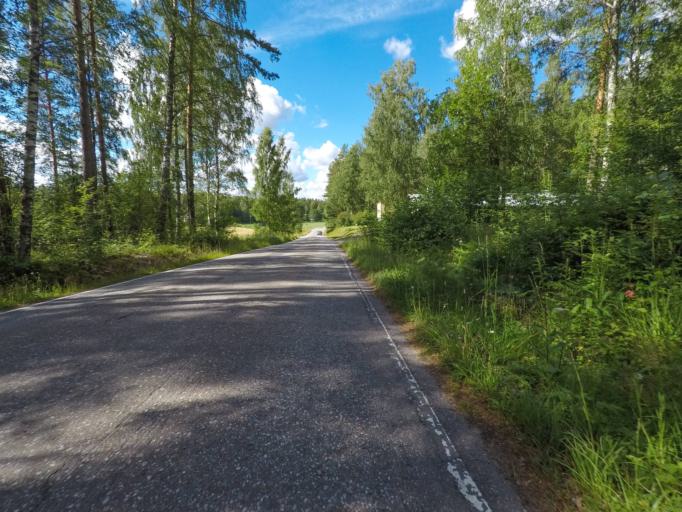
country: FI
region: South Karelia
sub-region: Lappeenranta
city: Joutseno
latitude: 61.1086
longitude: 28.3707
